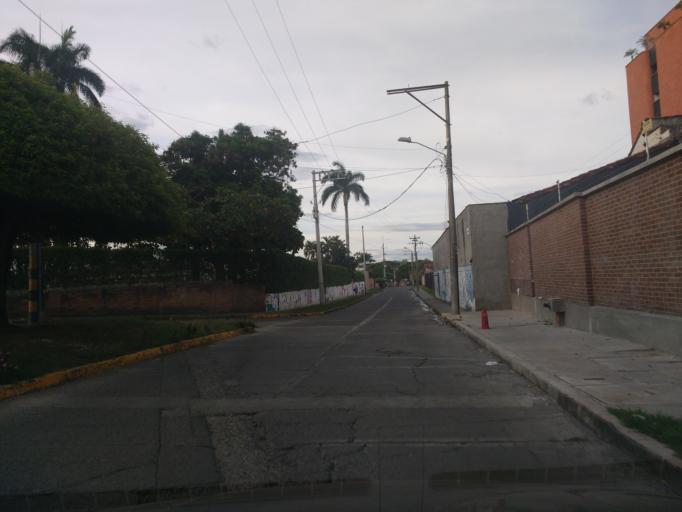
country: CO
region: Valle del Cauca
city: Cartago
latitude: 4.7555
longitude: -75.9196
